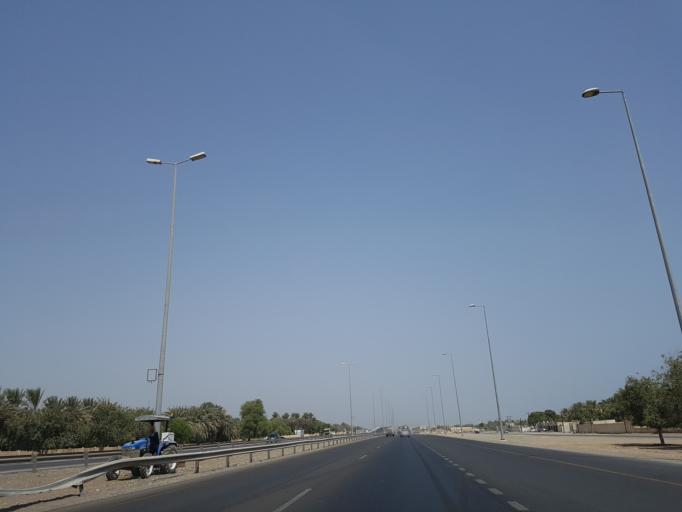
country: OM
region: Al Batinah
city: Saham
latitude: 24.0984
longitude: 56.9230
